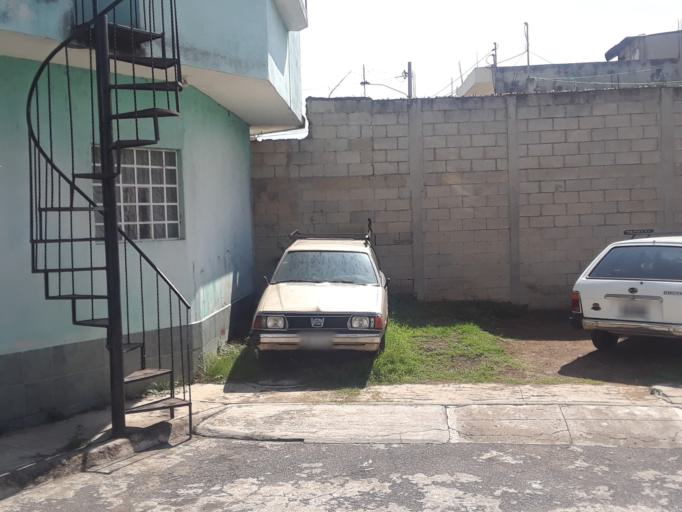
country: GT
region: Guatemala
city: Petapa
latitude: 14.5349
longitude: -90.5517
